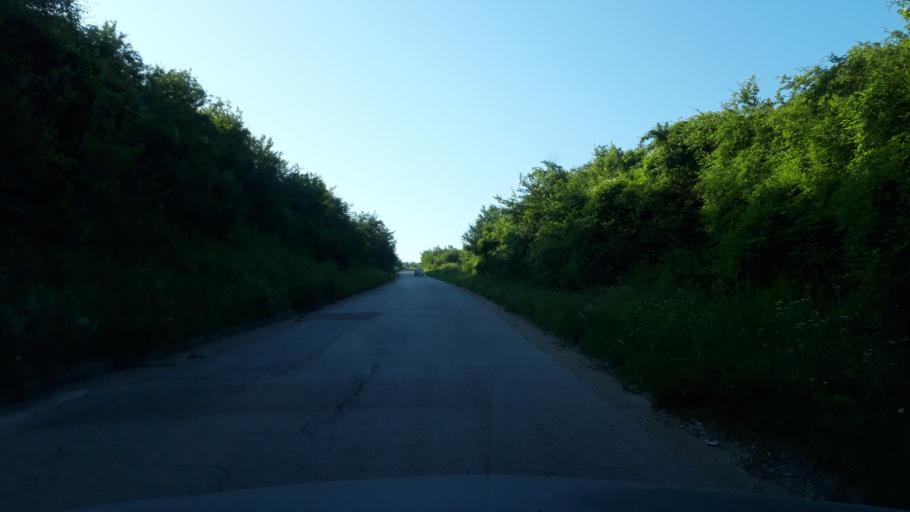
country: RS
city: Celarevo
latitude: 45.1256
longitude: 19.5082
